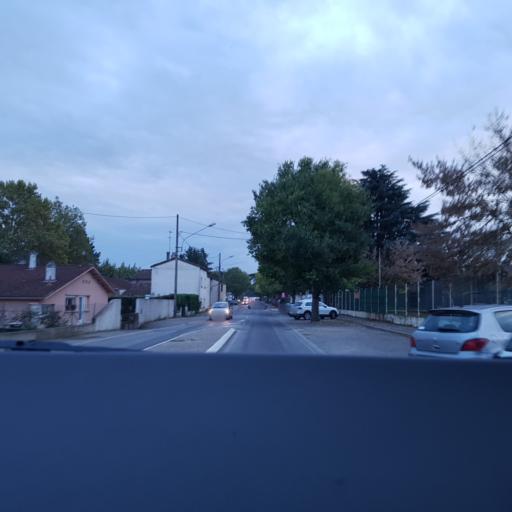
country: FR
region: Midi-Pyrenees
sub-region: Departement du Gers
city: Condom
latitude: 43.9495
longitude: 0.3627
